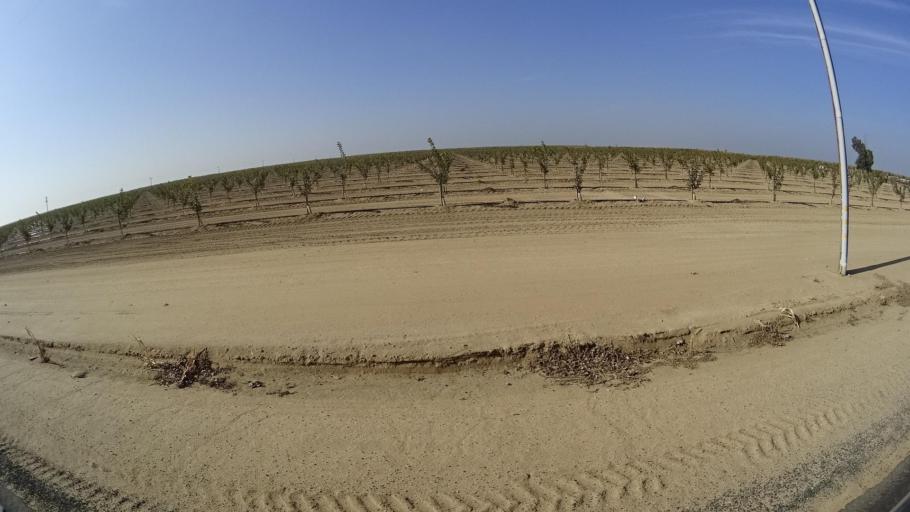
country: US
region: California
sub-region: Kern County
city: Shafter
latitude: 35.5463
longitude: -119.1514
